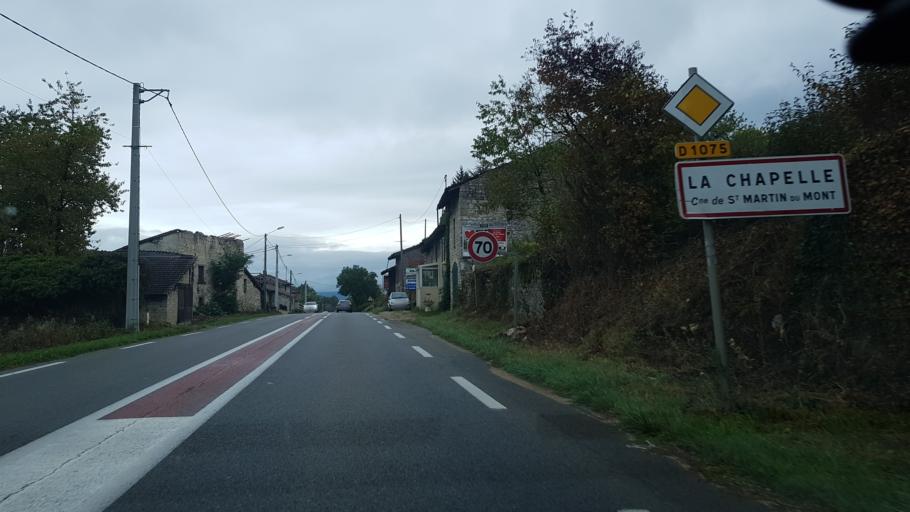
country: FR
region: Rhone-Alpes
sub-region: Departement de l'Ain
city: Saint-Martin-du-Mont
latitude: 46.0837
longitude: 5.3183
